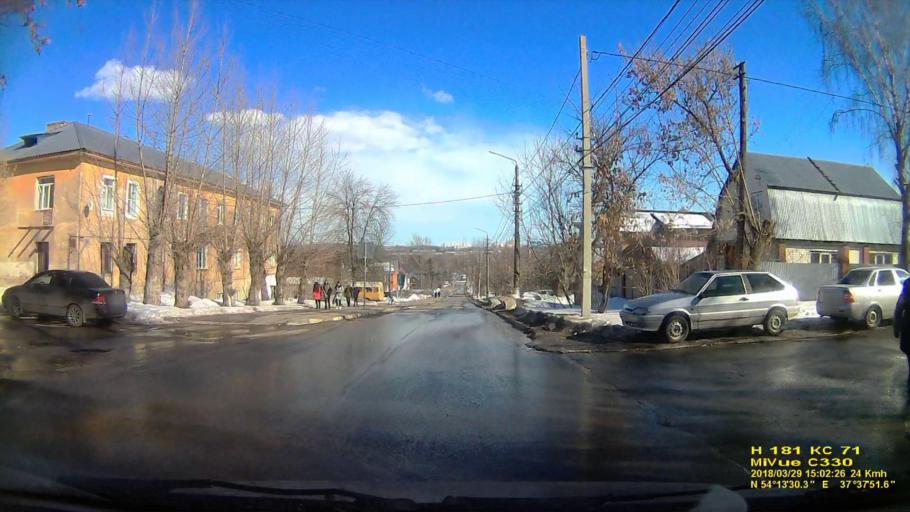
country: RU
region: Tula
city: Tula
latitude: 54.2251
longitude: 37.6311
